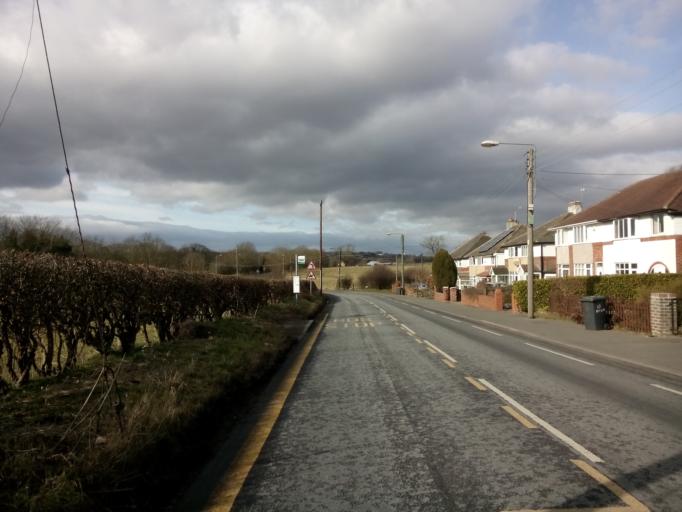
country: GB
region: England
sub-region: County Durham
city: Durham
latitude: 54.7777
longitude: -1.6009
